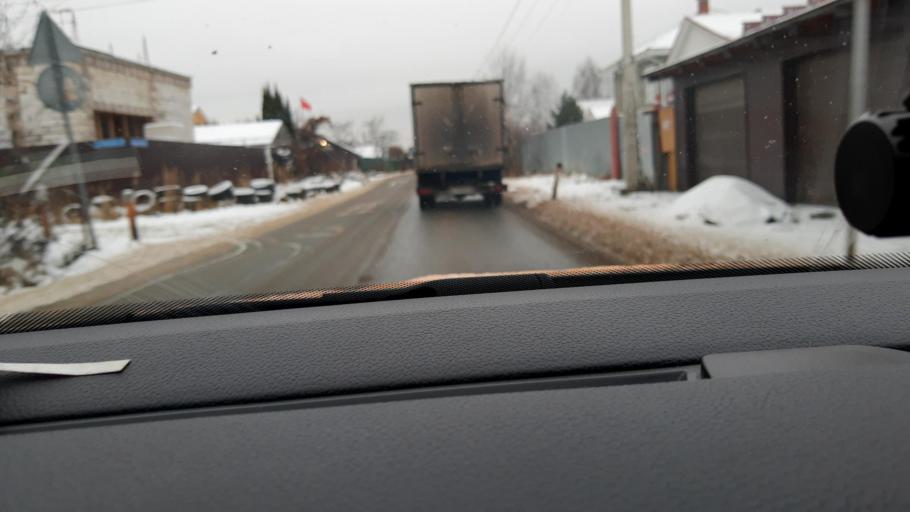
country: RU
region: Moskovskaya
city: Povedniki
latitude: 55.9305
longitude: 37.6346
